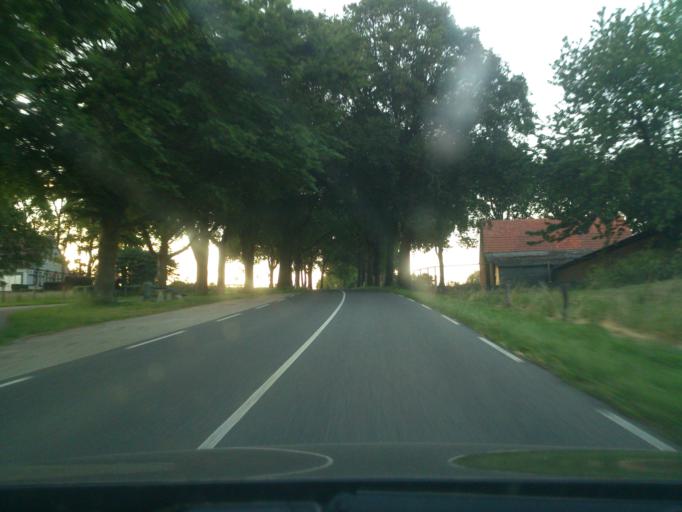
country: NL
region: Gelderland
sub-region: Gemeente Groesbeek
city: Groesbeek
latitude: 51.7952
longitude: 5.9301
